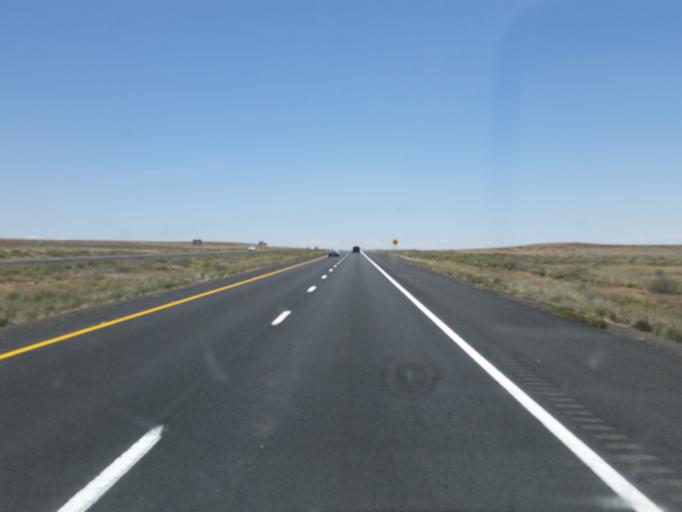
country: US
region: Arizona
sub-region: Coconino County
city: LeChee
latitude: 35.1171
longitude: -111.0893
